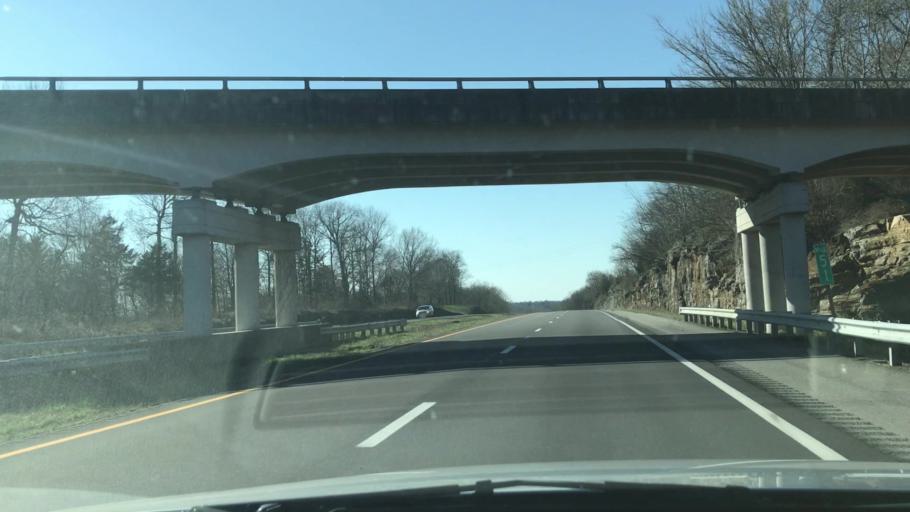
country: US
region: Kentucky
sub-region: Adair County
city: Columbia
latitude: 37.0872
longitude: -85.2658
